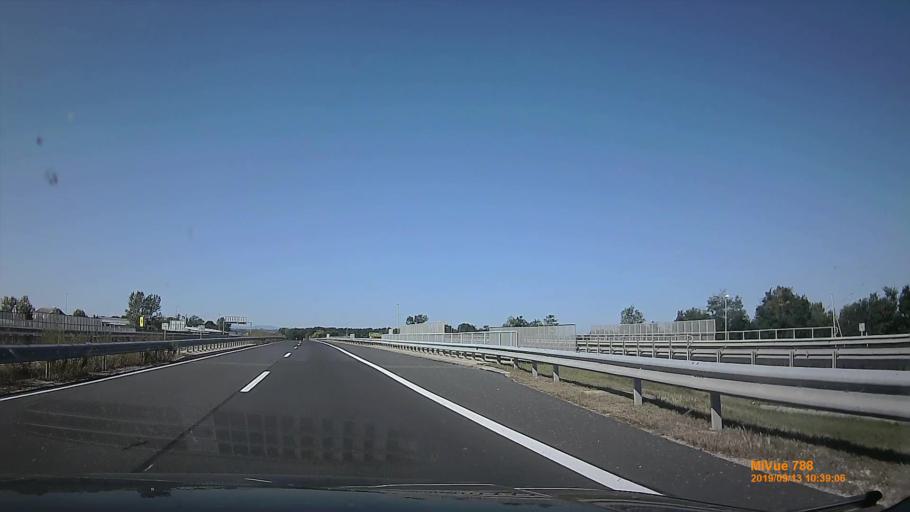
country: SI
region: Murska Sobota
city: Krog
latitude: 46.6350
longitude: 16.1589
